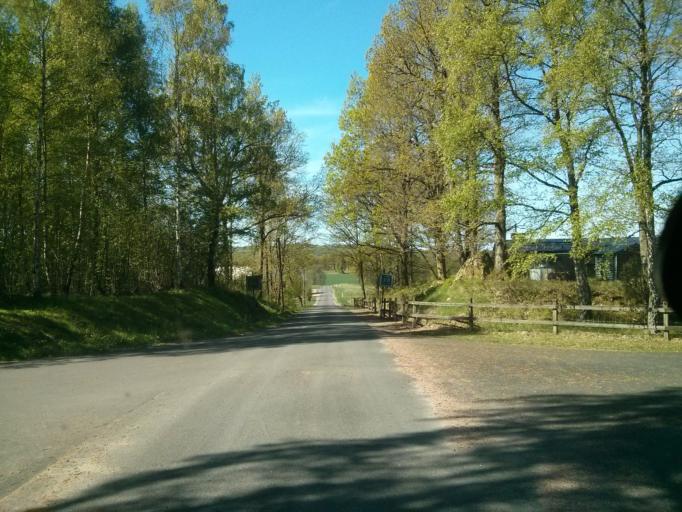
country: SE
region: Halland
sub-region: Halmstads Kommun
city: Aled
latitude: 56.7610
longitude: 12.8637
